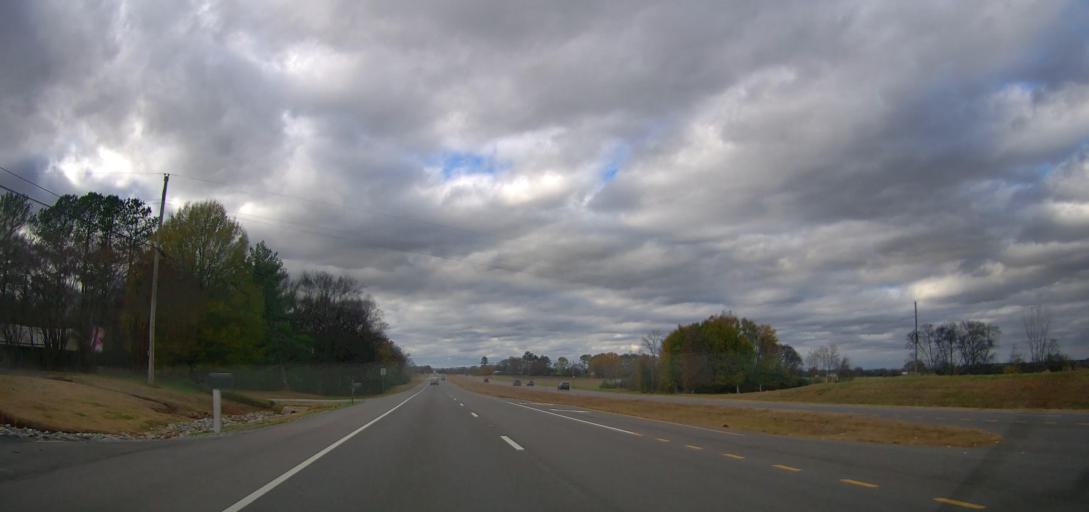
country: US
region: Alabama
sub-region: Lawrence County
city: Moulton
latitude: 34.4431
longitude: -87.2103
